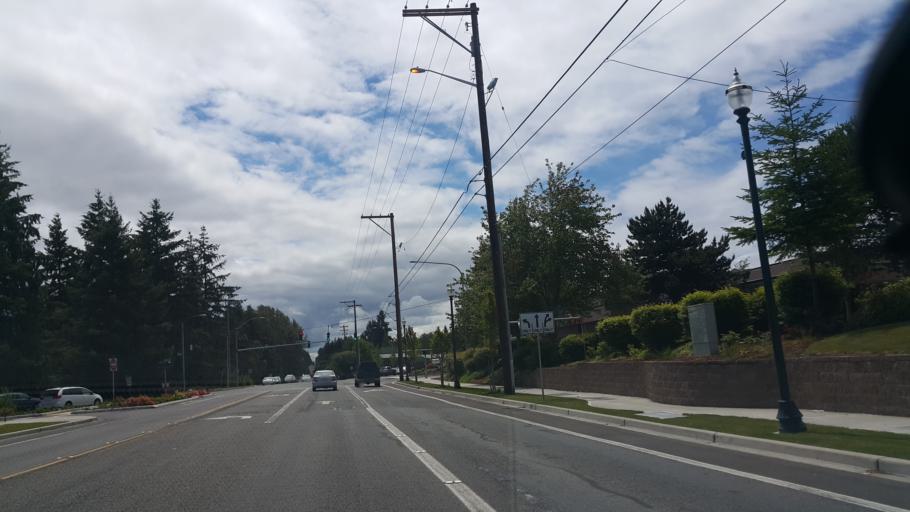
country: US
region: Washington
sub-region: Pierce County
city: Fircrest
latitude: 47.2385
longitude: -122.5265
